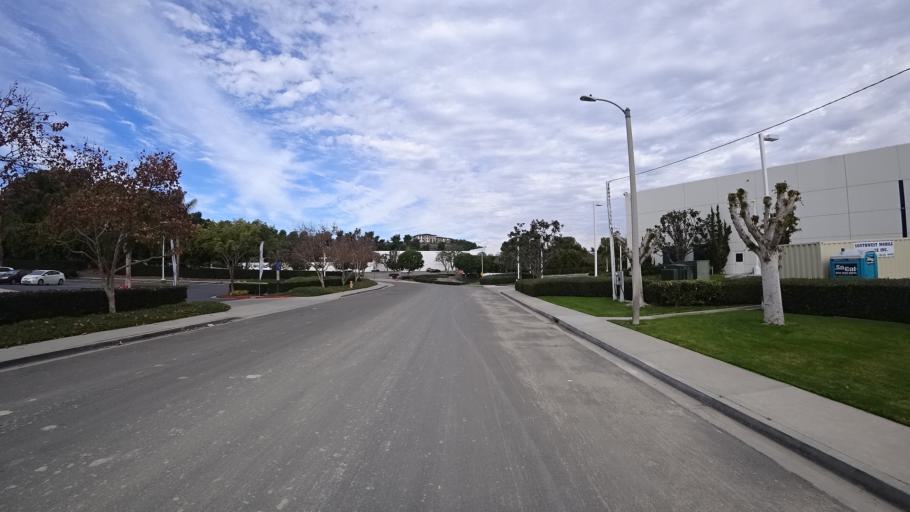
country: US
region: California
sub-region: Orange County
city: Aliso Viejo
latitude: 33.5580
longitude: -117.7266
